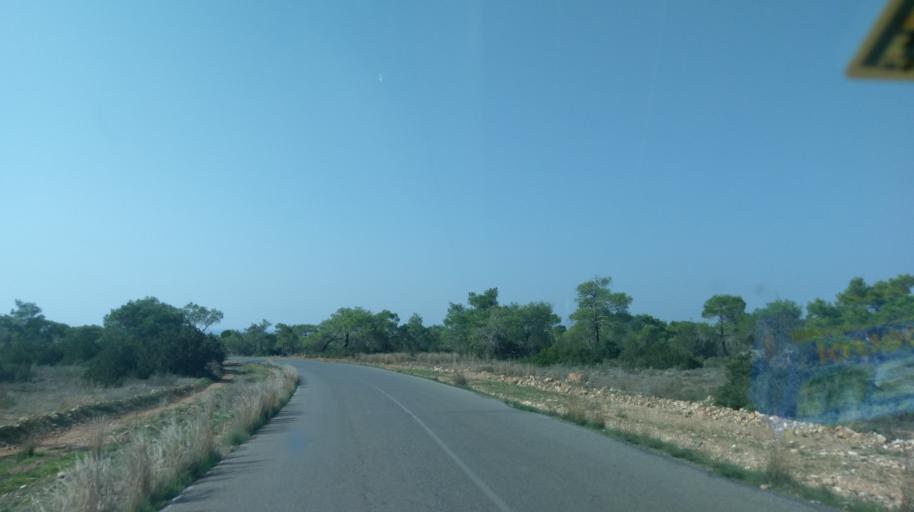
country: CY
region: Lefkosia
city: Morfou
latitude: 35.3002
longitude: 32.9840
